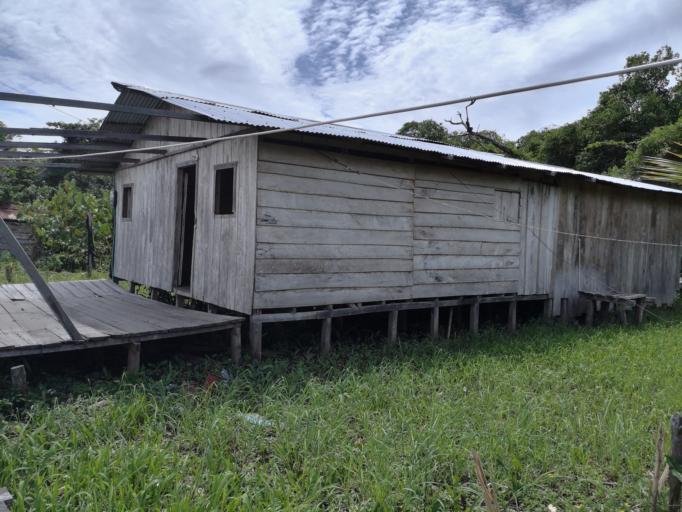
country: CO
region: Antioquia
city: Turbo
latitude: 8.0886
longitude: -76.8348
